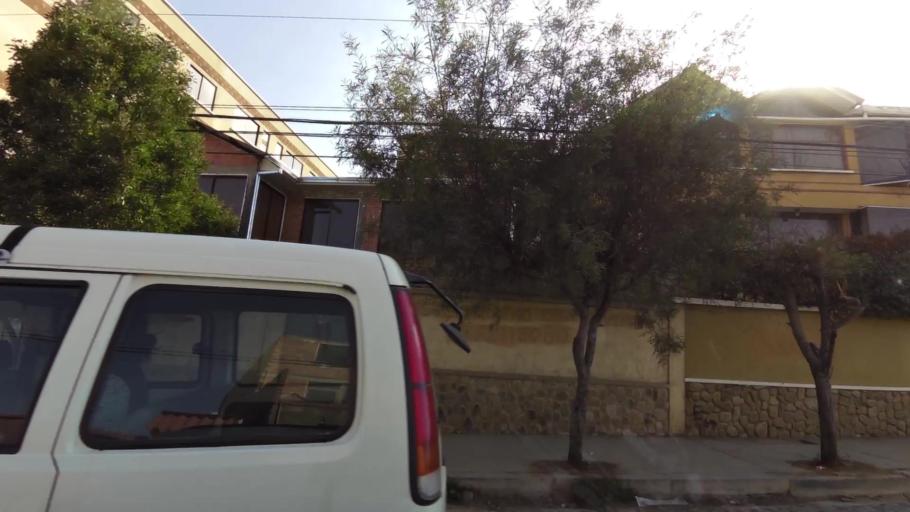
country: BO
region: La Paz
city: La Paz
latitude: -16.5180
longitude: -68.0838
